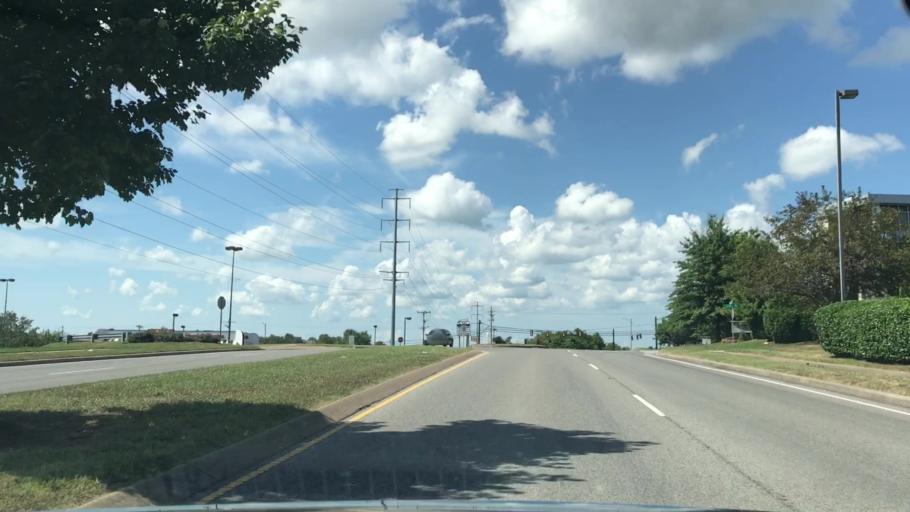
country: US
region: Tennessee
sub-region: Williamson County
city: Franklin
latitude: 35.9136
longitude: -86.8156
